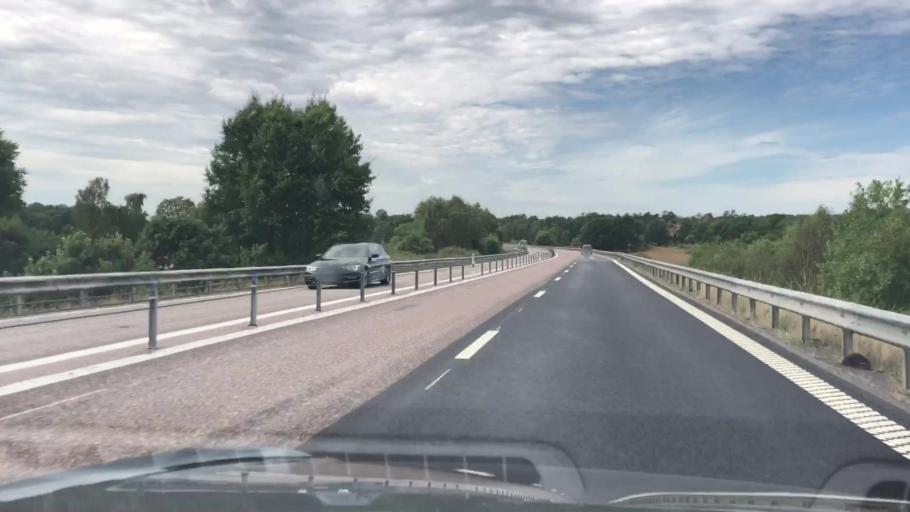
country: SE
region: Blekinge
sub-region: Ronneby Kommun
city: Brakne-Hoby
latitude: 56.2081
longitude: 15.0567
